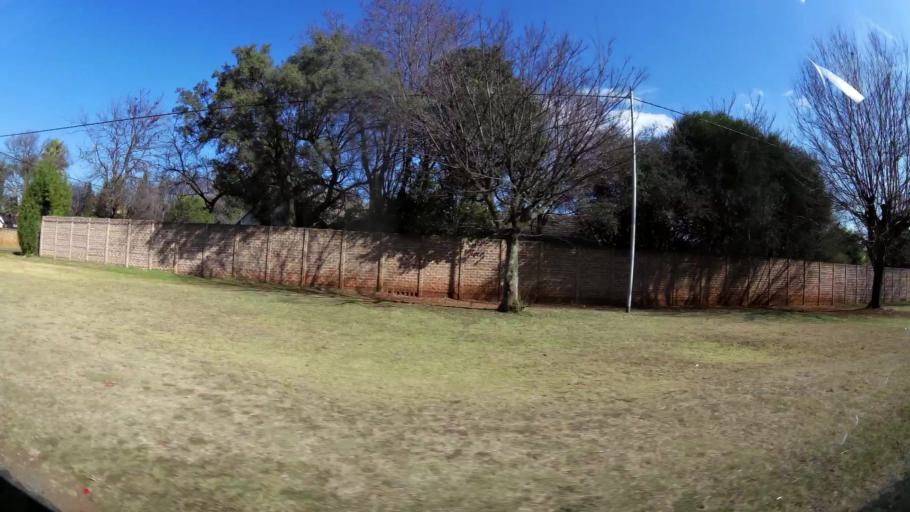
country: ZA
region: Gauteng
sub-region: Ekurhuleni Metropolitan Municipality
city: Benoni
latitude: -26.1515
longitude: 28.3325
